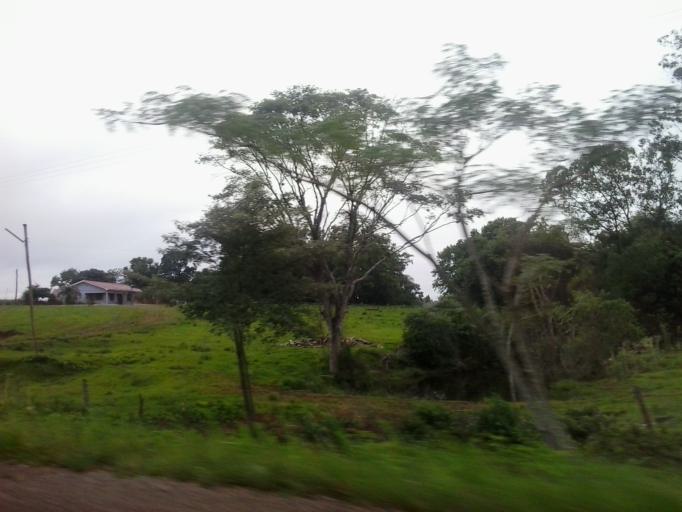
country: BR
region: Rio Grande do Sul
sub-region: Santa Maria
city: Santa Maria
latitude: -29.7226
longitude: -53.3696
